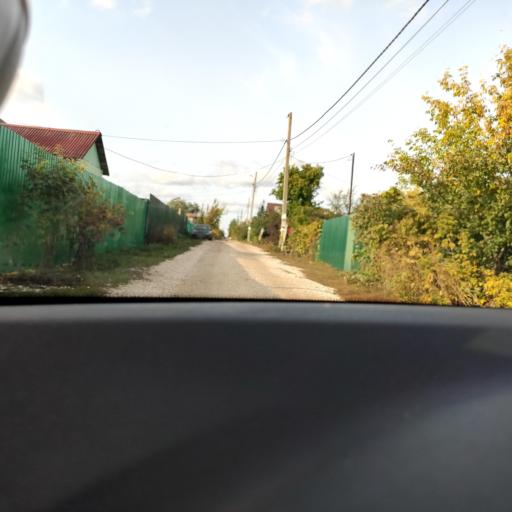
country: RU
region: Samara
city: Petra-Dubrava
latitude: 53.2812
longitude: 50.2957
